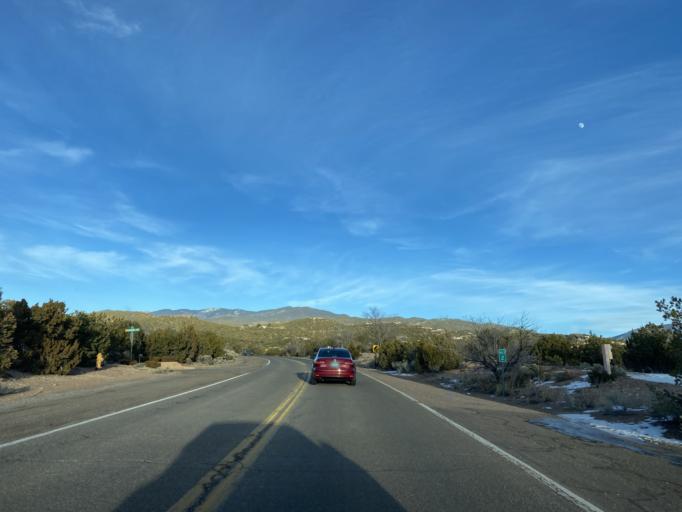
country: US
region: New Mexico
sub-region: Santa Fe County
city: Santa Fe
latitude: 35.6933
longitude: -105.9215
